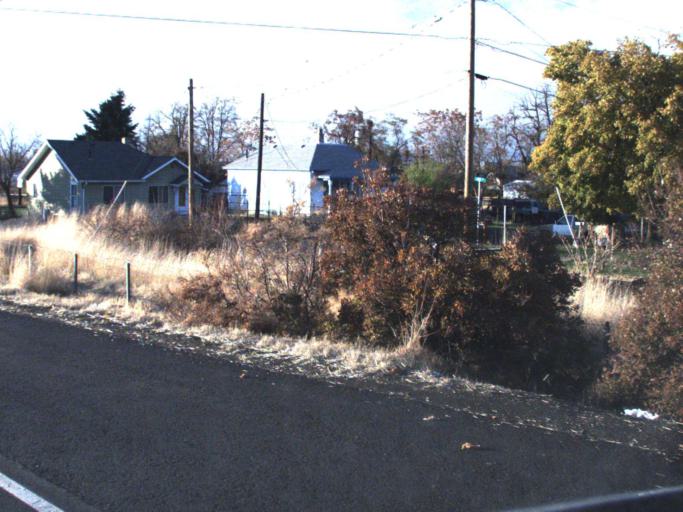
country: US
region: Washington
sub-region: Walla Walla County
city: Walla Walla
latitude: 46.0697
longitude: -118.3607
